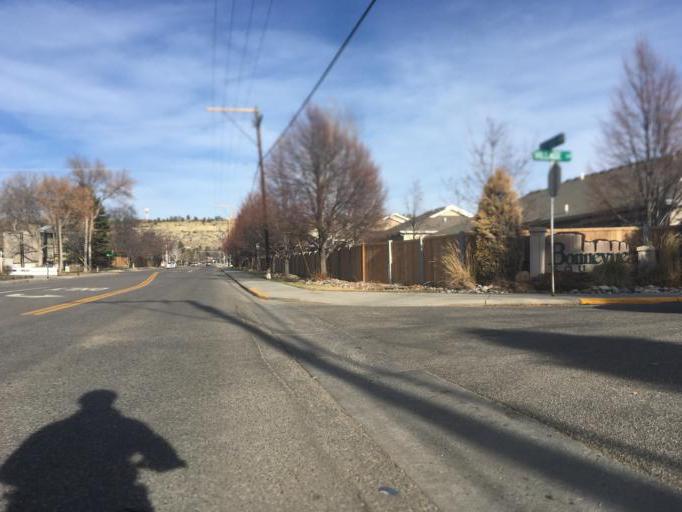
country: US
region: Montana
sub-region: Yellowstone County
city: Billings
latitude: 45.7928
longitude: -108.5590
